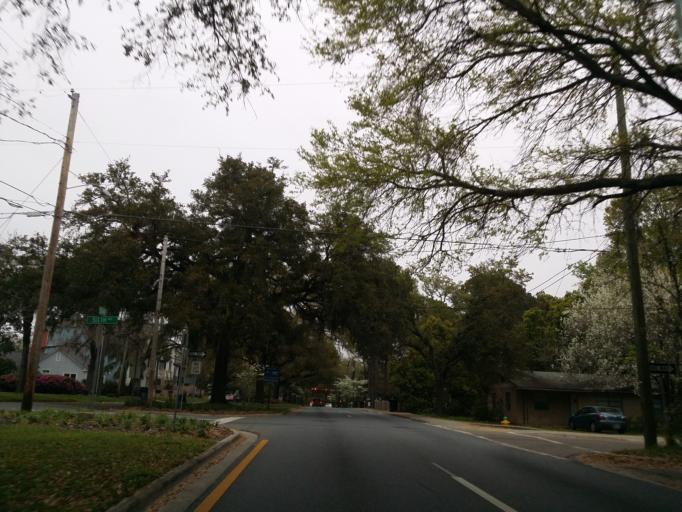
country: US
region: Florida
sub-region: Leon County
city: Tallahassee
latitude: 30.4562
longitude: -84.2831
